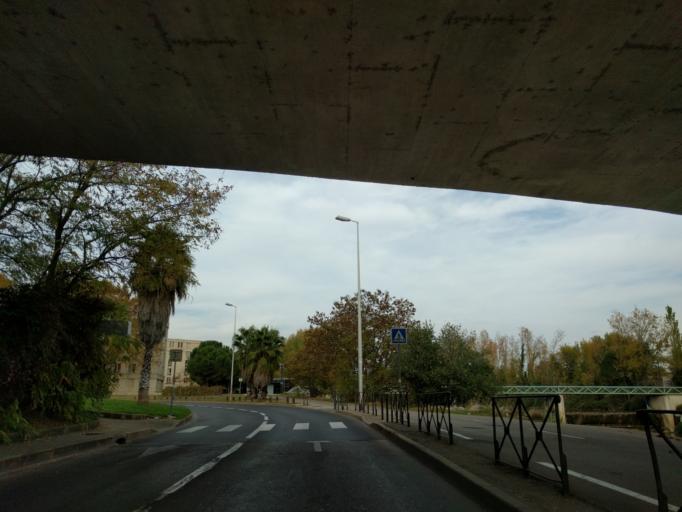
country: FR
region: Languedoc-Roussillon
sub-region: Departement de l'Herault
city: Montpellier
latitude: 43.6090
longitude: 3.8968
